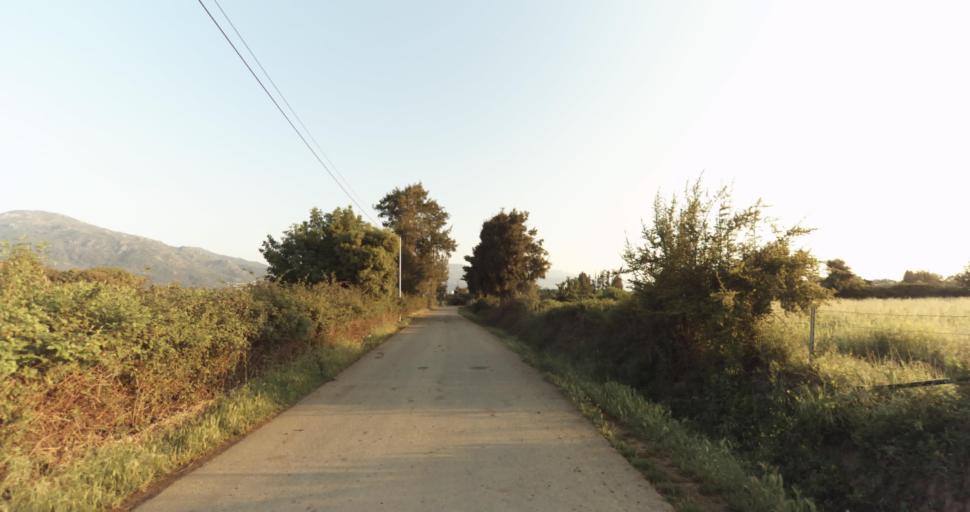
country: FR
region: Corsica
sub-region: Departement de la Haute-Corse
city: Biguglia
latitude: 42.6005
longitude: 9.4543
